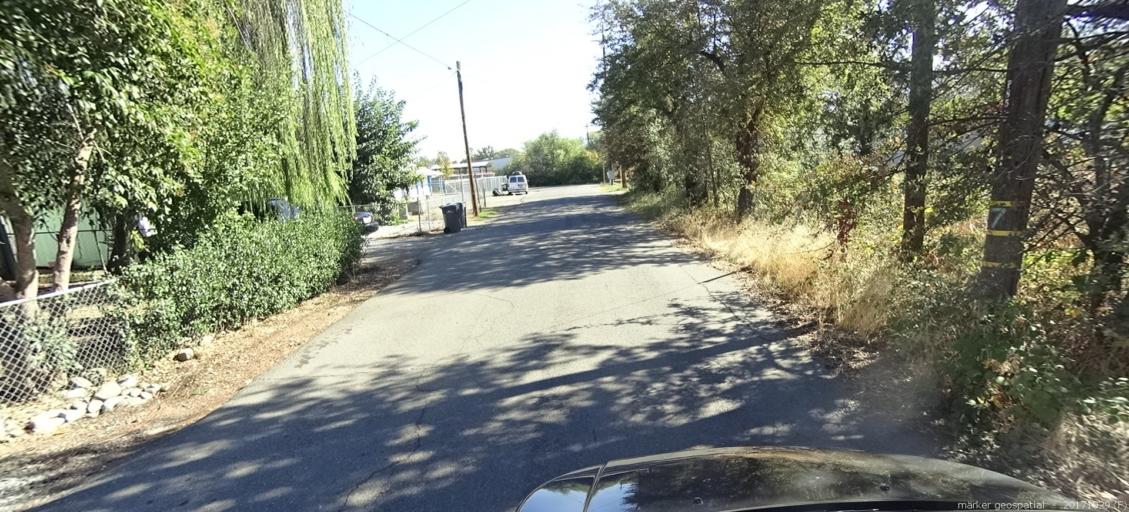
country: US
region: California
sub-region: Shasta County
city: Anderson
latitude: 40.4865
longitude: -122.3566
